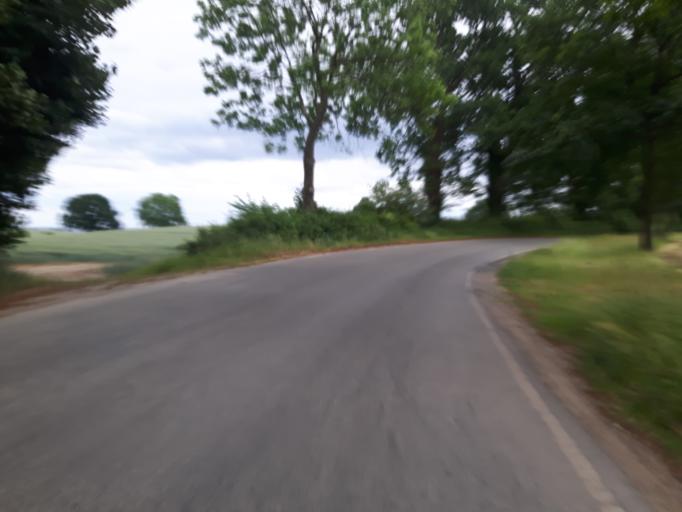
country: DE
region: Schleswig-Holstein
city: Schashagen
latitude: 54.1124
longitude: 10.9023
